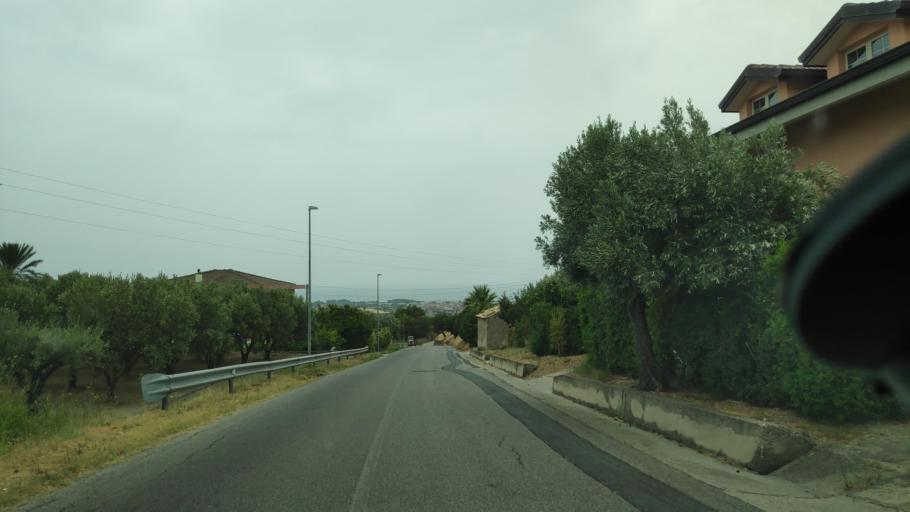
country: IT
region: Calabria
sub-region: Provincia di Catanzaro
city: Martelli-Laganosa
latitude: 38.6667
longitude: 16.5160
